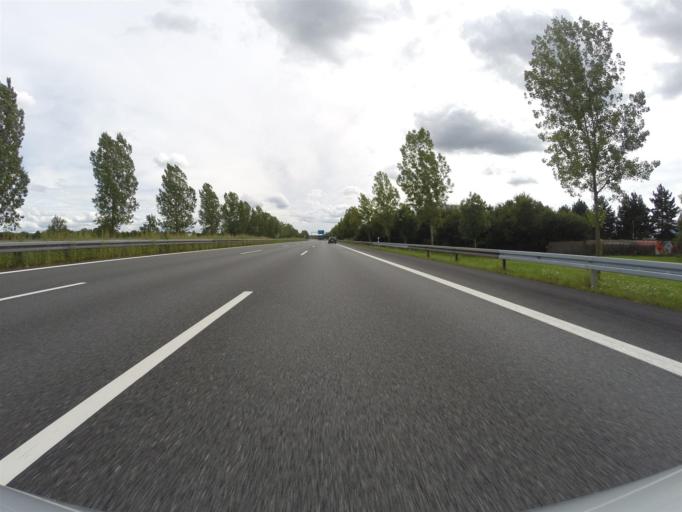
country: DE
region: Bavaria
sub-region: Upper Franconia
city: Bindlach
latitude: 49.9732
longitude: 11.6060
